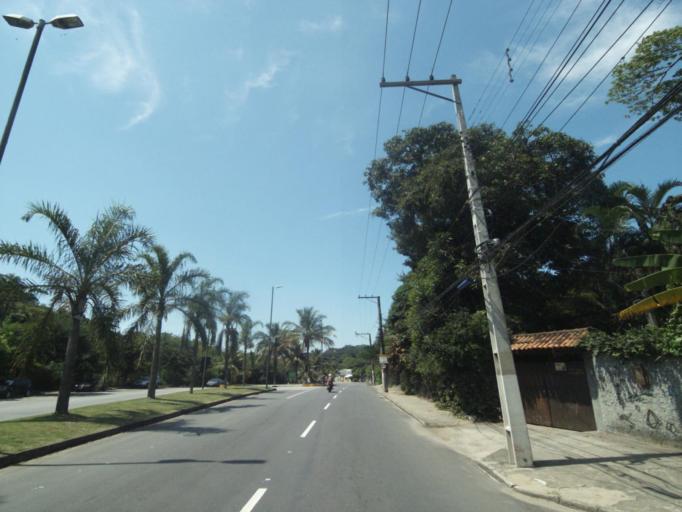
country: BR
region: Rio de Janeiro
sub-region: Niteroi
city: Niteroi
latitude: -22.9020
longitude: -43.0439
